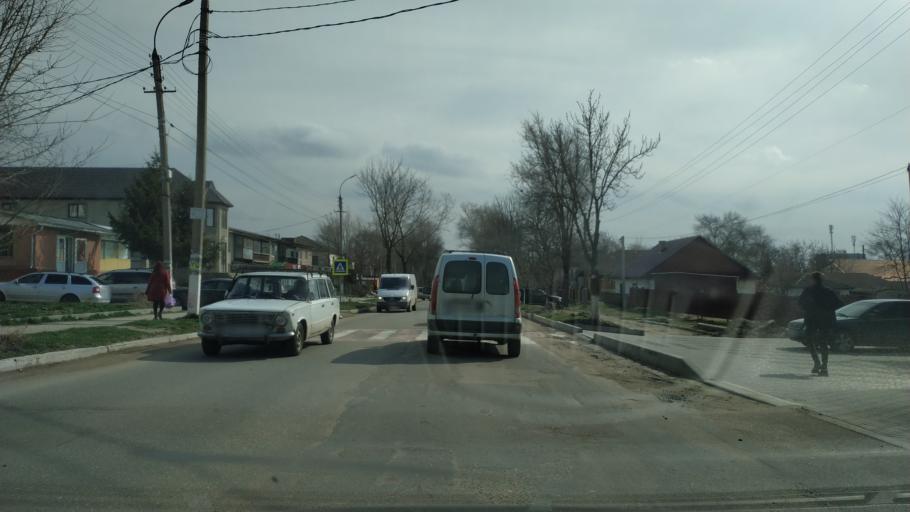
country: MD
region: Gagauzia
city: Vulcanesti
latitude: 45.6869
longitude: 28.4039
